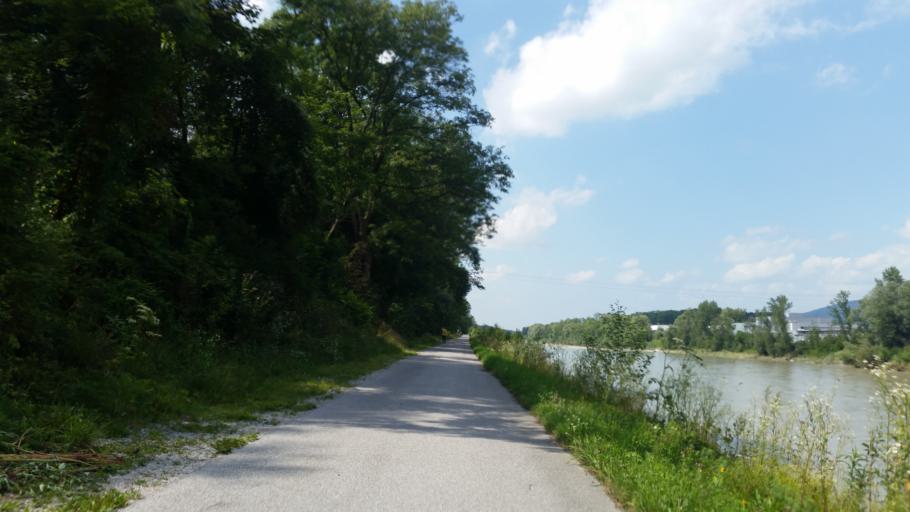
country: AT
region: Salzburg
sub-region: Politischer Bezirk Salzburg-Umgebung
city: Bergheim
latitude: 47.8420
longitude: 13.0149
